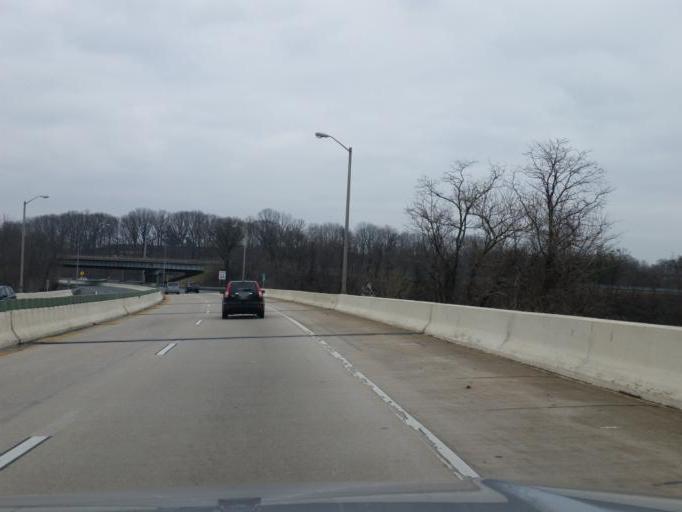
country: US
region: Maryland
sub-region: Anne Arundel County
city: Brooklyn Park
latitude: 39.2284
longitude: -76.6268
